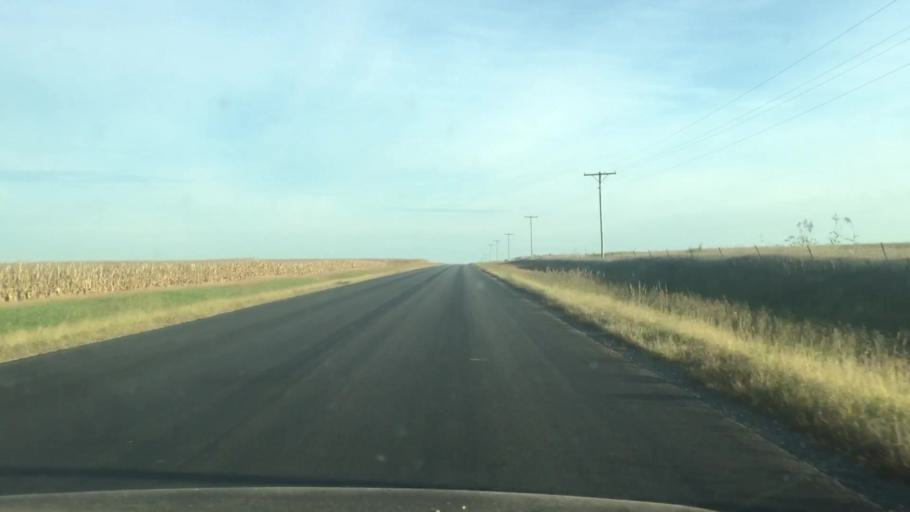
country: US
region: Kansas
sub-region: Marshall County
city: Marysville
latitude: 39.9155
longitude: -96.6009
